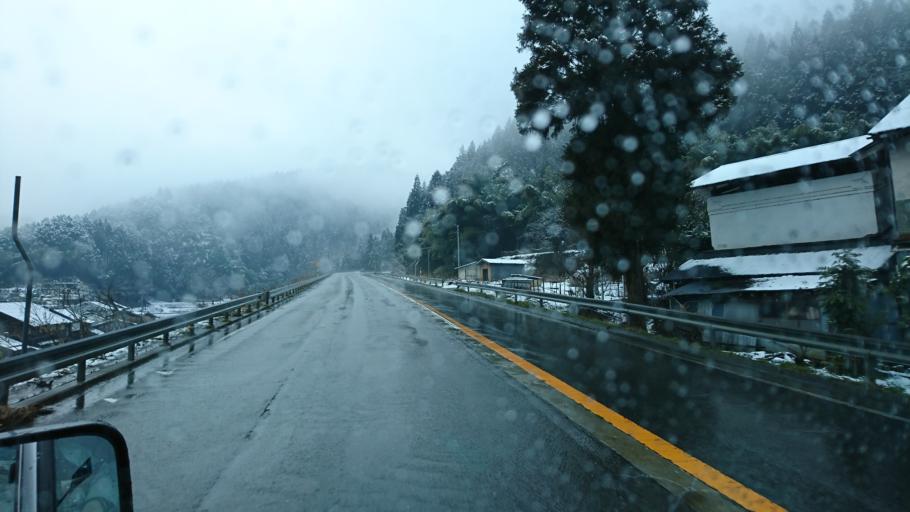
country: JP
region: Hyogo
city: Toyooka
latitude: 35.4891
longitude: 134.5550
